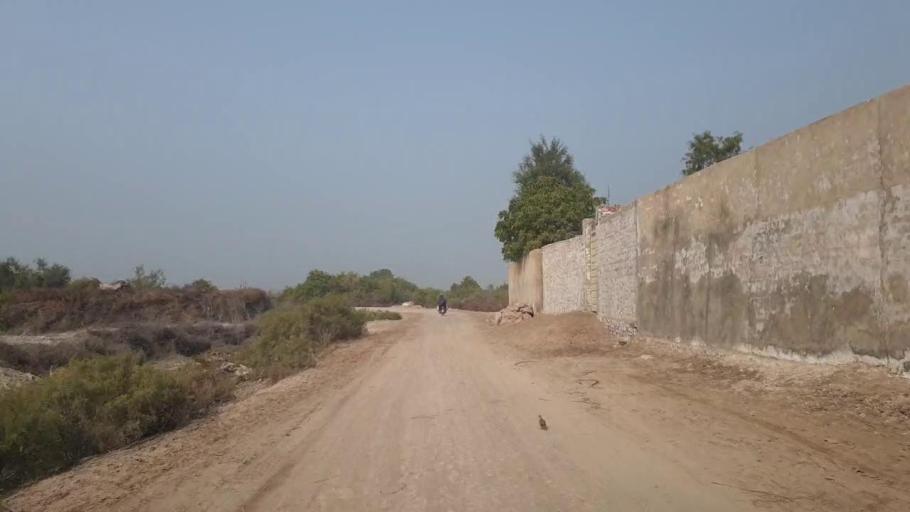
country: PK
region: Sindh
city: Bhit Shah
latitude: 25.8540
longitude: 68.5649
